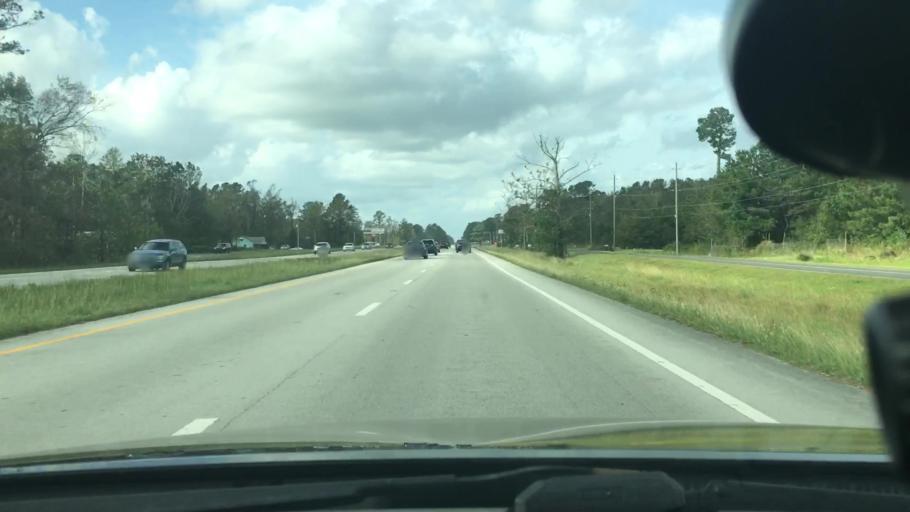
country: US
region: North Carolina
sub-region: Craven County
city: Neuse Forest
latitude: 35.0056
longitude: -76.9894
